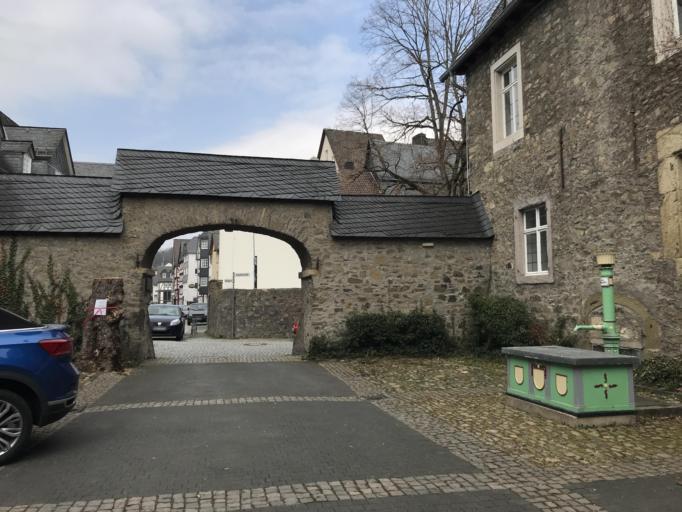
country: DE
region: Hesse
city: Herborn
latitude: 50.6825
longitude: 8.3027
